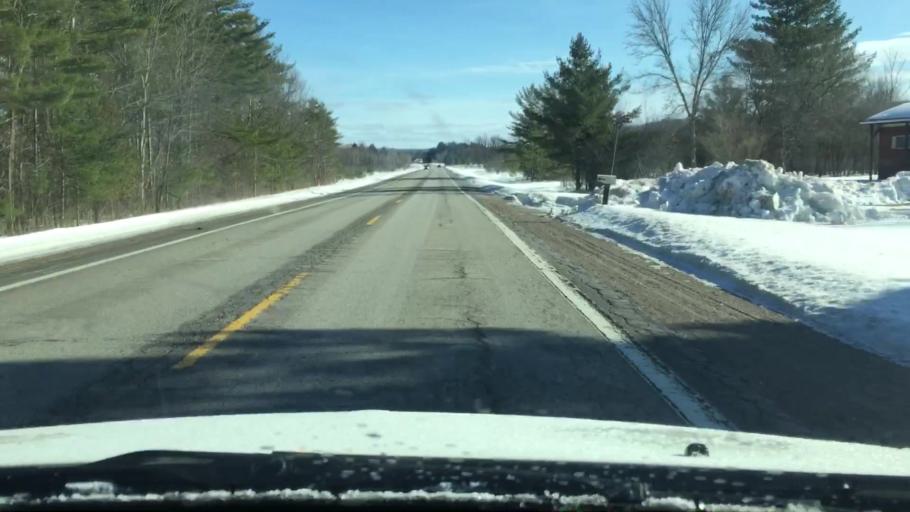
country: US
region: Michigan
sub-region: Charlevoix County
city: East Jordan
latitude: 45.1037
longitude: -85.1203
